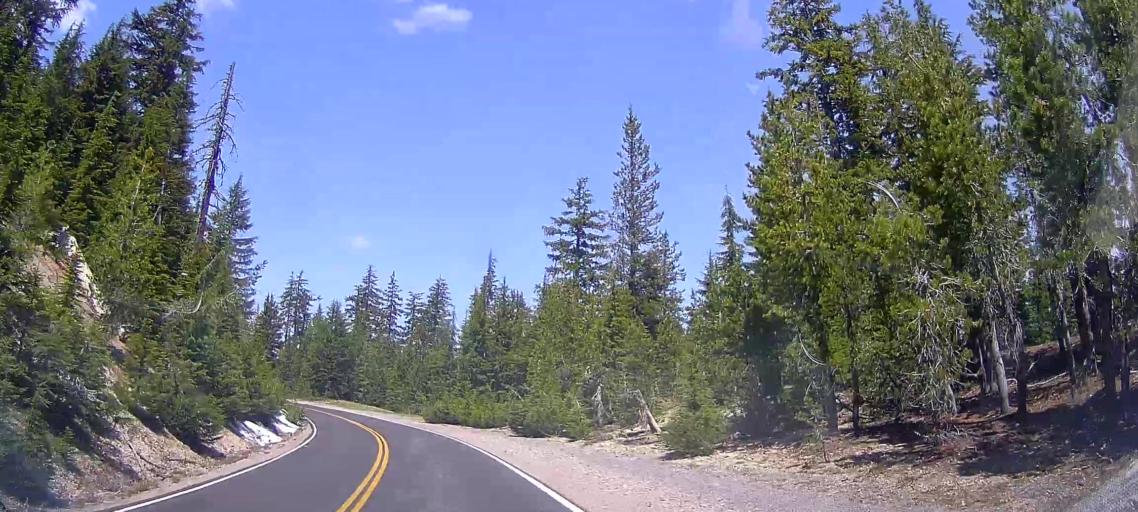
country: US
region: Oregon
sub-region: Jackson County
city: Shady Cove
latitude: 42.9810
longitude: -122.1084
